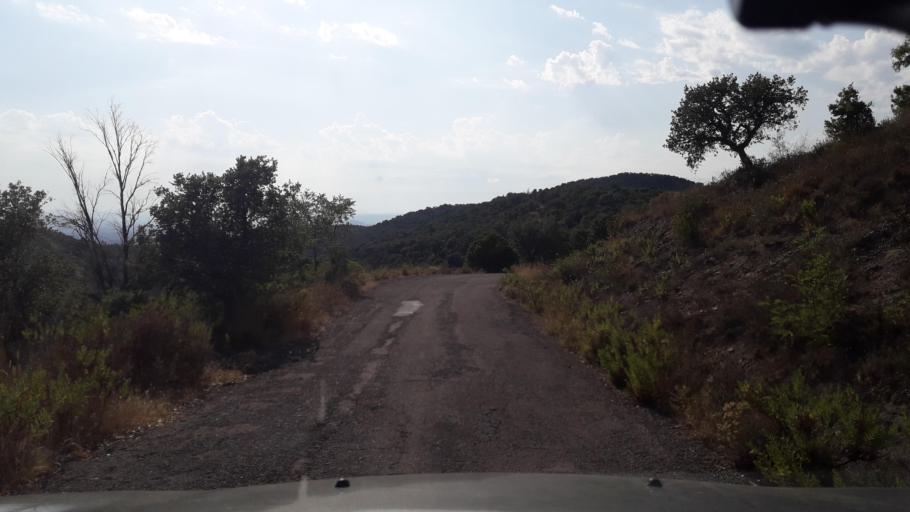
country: FR
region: Provence-Alpes-Cote d'Azur
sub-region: Departement du Var
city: Saint-Raphael
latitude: 43.5007
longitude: 6.7964
